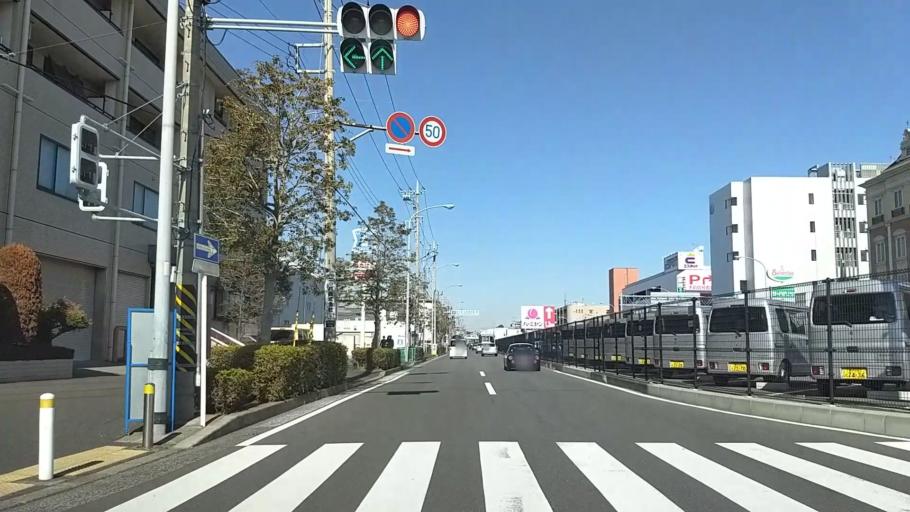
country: JP
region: Kanagawa
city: Yokohama
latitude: 35.5164
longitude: 139.6129
